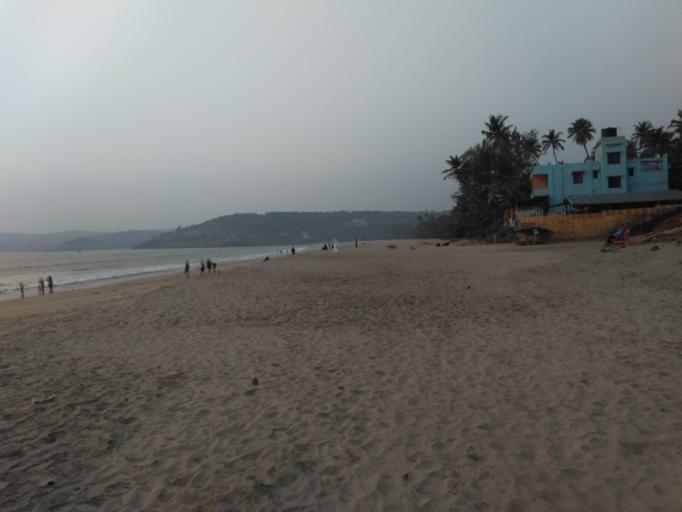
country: IN
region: Maharashtra
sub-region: Ratnagiri
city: Guhagar
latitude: 17.3784
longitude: 73.2097
